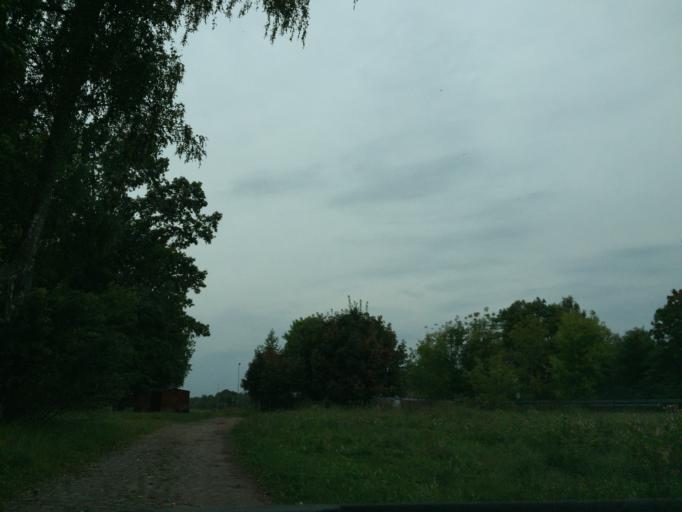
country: LV
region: Zilupes
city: Zilupe
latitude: 56.3917
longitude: 28.1114
